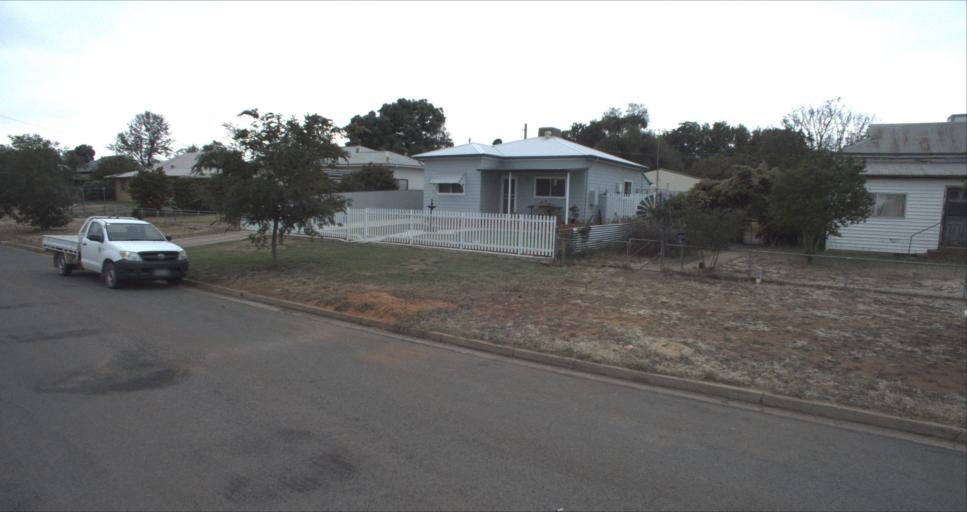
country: AU
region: New South Wales
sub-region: Leeton
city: Leeton
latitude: -34.5535
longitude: 146.4008
